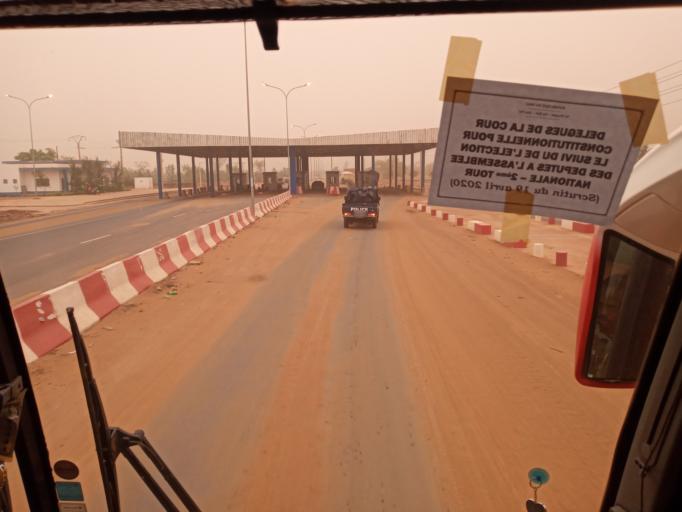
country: ML
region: Koulikoro
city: Koulikoro
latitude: 12.8150
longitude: -7.6527
